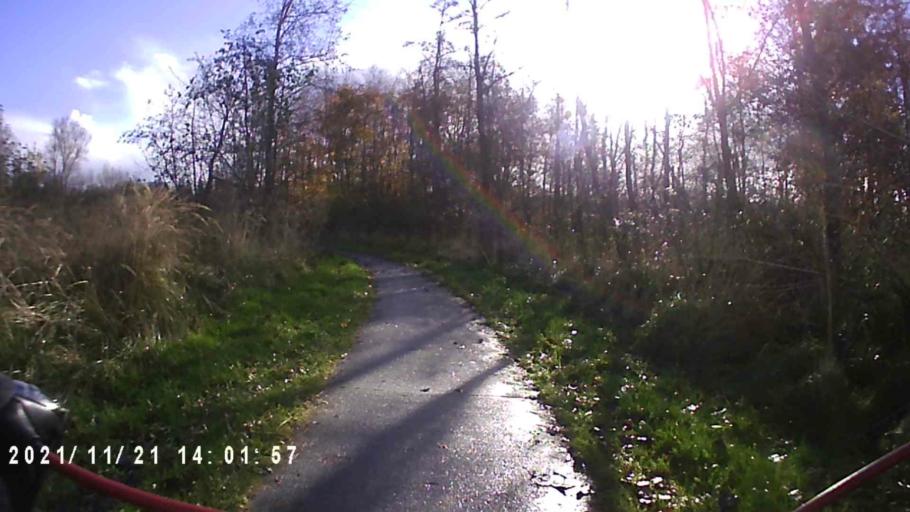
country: NL
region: Groningen
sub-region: Gemeente De Marne
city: Ulrum
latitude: 53.3930
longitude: 6.2403
